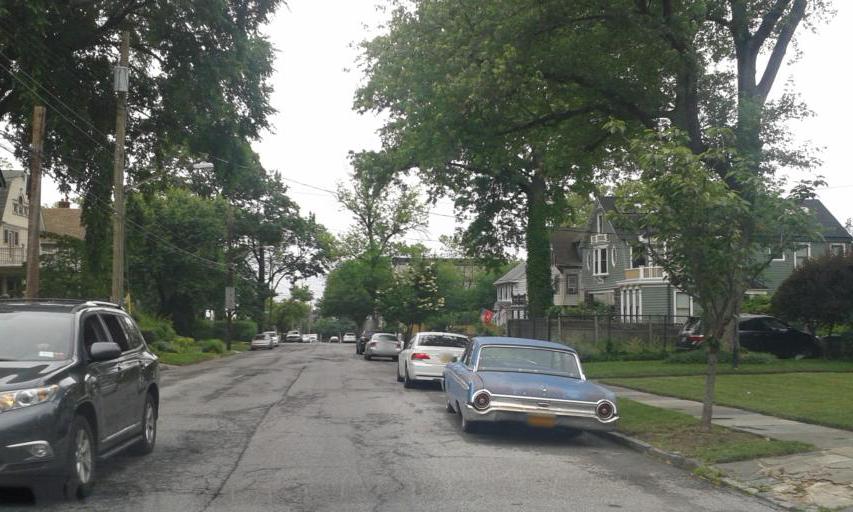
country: US
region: New Jersey
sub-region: Hudson County
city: Bayonne
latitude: 40.6422
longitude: -74.0981
